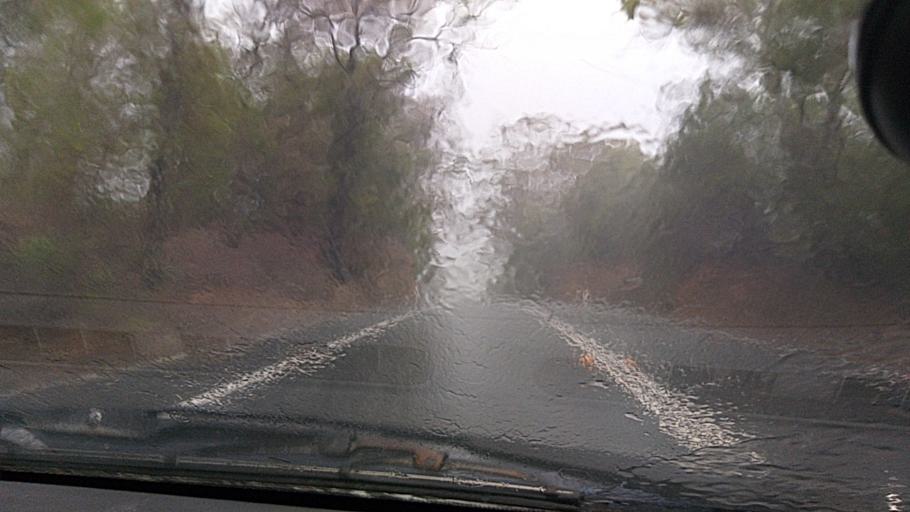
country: AU
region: New South Wales
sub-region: Camden
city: Camden South
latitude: -34.1298
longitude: 150.7046
